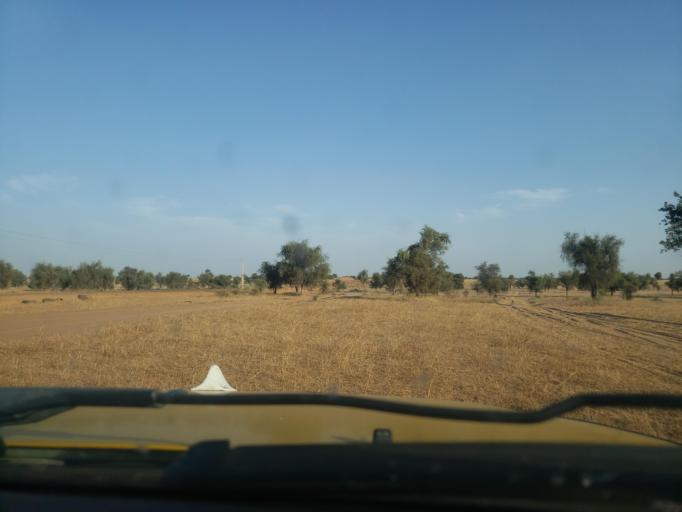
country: SN
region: Louga
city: Dara
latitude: 15.4285
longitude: -15.7464
